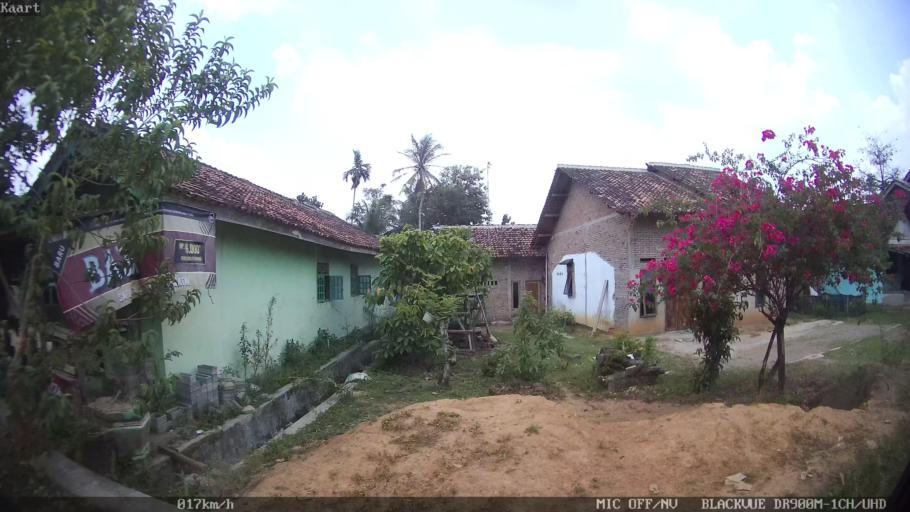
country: ID
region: Lampung
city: Pringsewu
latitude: -5.3430
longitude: 104.9791
